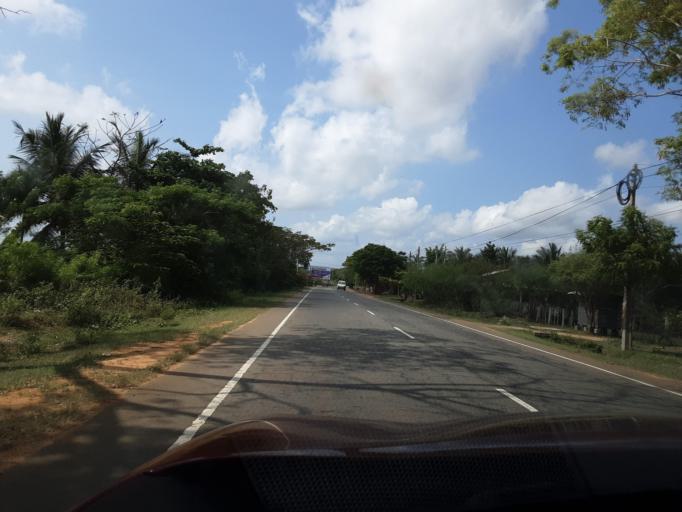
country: LK
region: Southern
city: Tangalla
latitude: 6.2425
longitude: 81.2269
